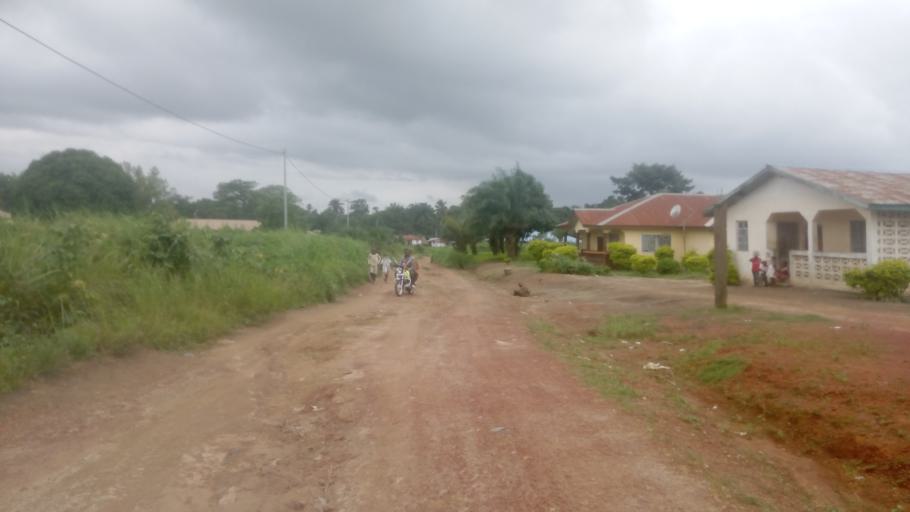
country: SL
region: Northern Province
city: Lunsar
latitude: 8.6839
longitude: -12.5493
